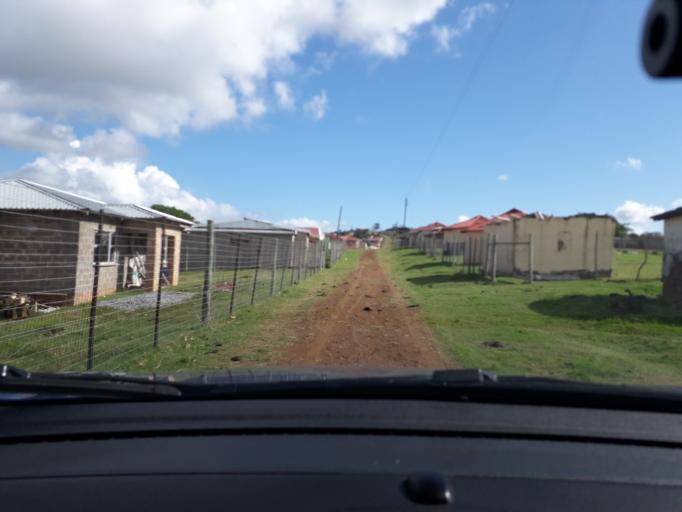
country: ZA
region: Eastern Cape
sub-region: Buffalo City Metropolitan Municipality
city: Bhisho
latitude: -33.1146
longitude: 27.4372
